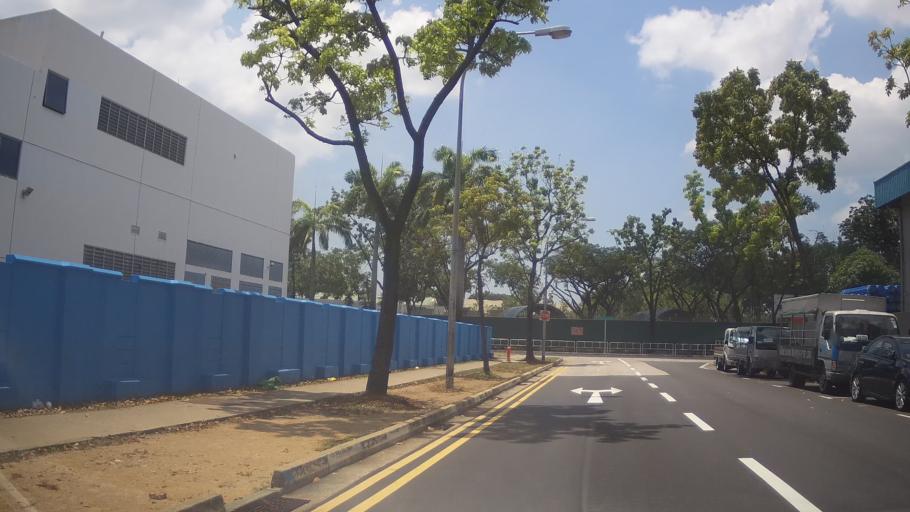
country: SG
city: Singapore
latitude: 1.2954
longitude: 103.6666
